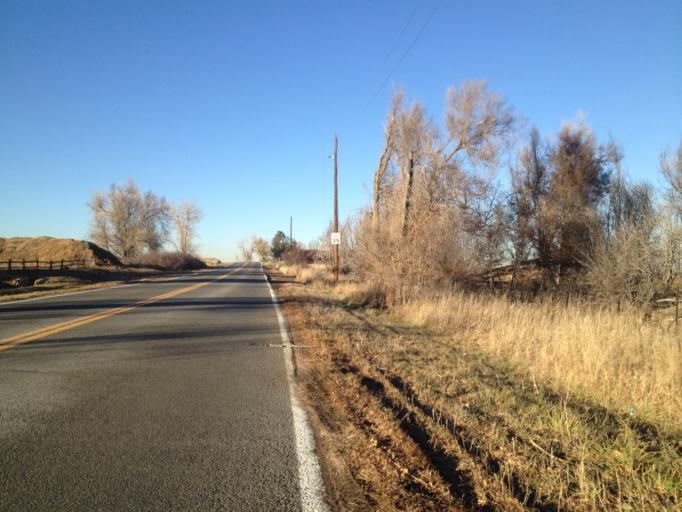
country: US
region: Colorado
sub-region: Boulder County
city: Louisville
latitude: 39.9734
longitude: -105.1092
